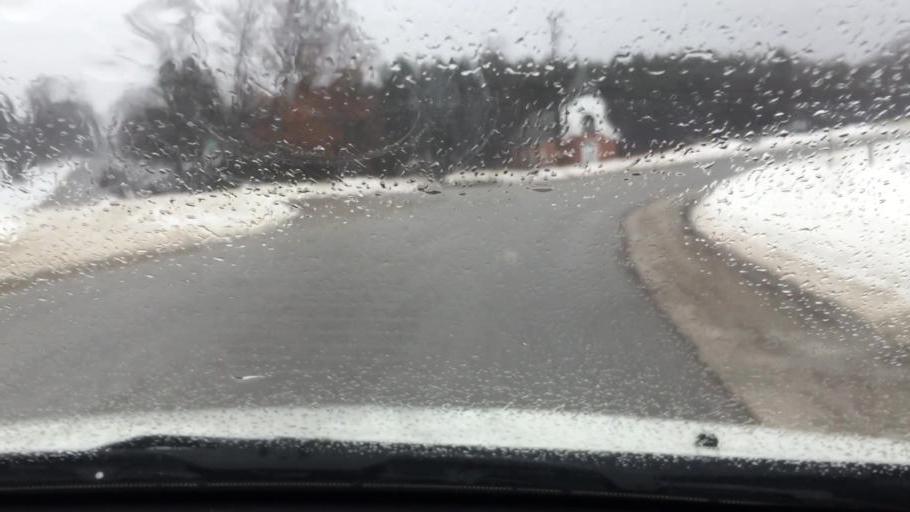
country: US
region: Michigan
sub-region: Charlevoix County
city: East Jordan
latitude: 45.1053
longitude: -85.1596
